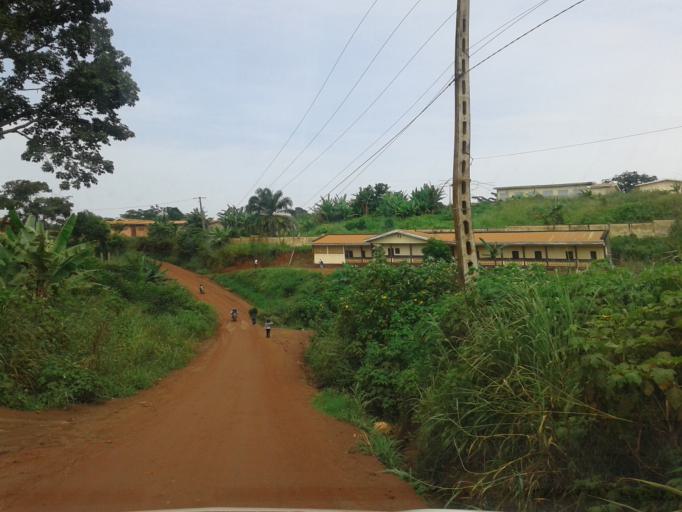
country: CM
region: Centre
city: Yaounde
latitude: 3.9237
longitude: 11.5071
